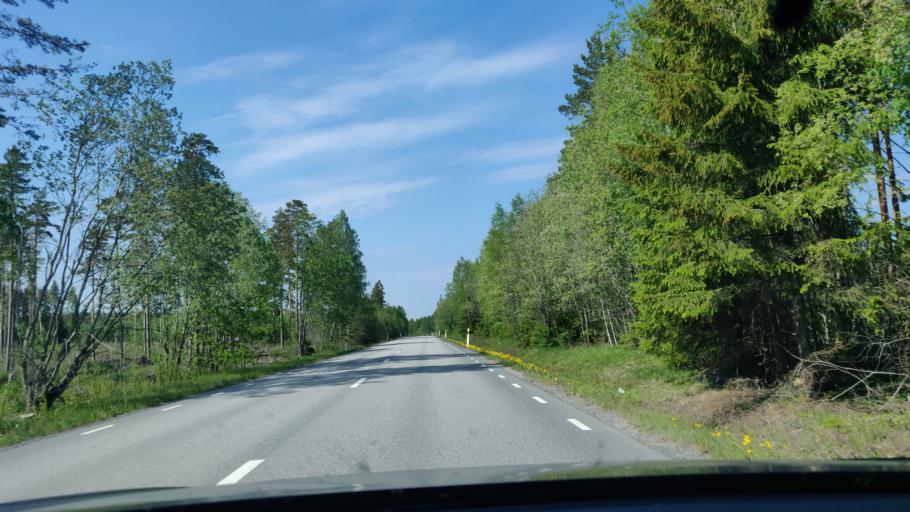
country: SE
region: Uppsala
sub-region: Heby Kommun
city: OEstervala
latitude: 60.1351
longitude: 17.2182
